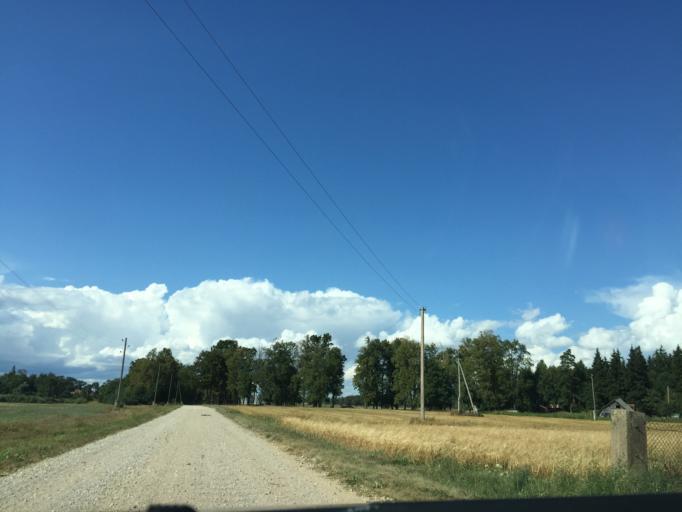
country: LT
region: Siauliu apskritis
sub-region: Joniskis
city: Joniskis
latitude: 56.3386
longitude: 23.5569
